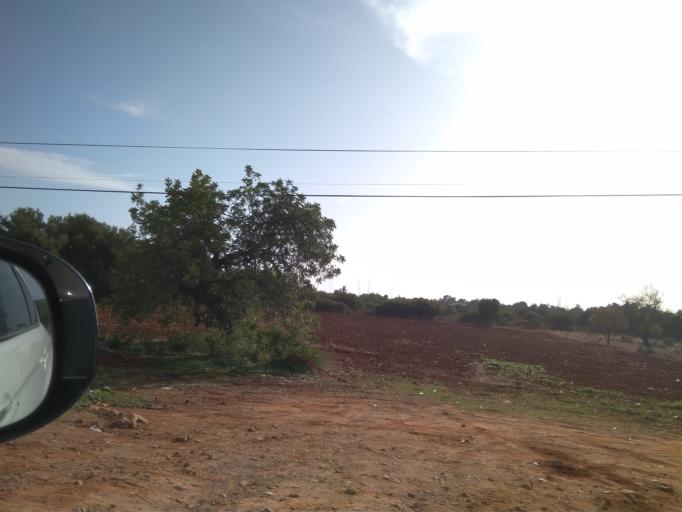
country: PT
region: Faro
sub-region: Faro
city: Santa Barbara de Nexe
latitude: 37.0939
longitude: -7.9457
